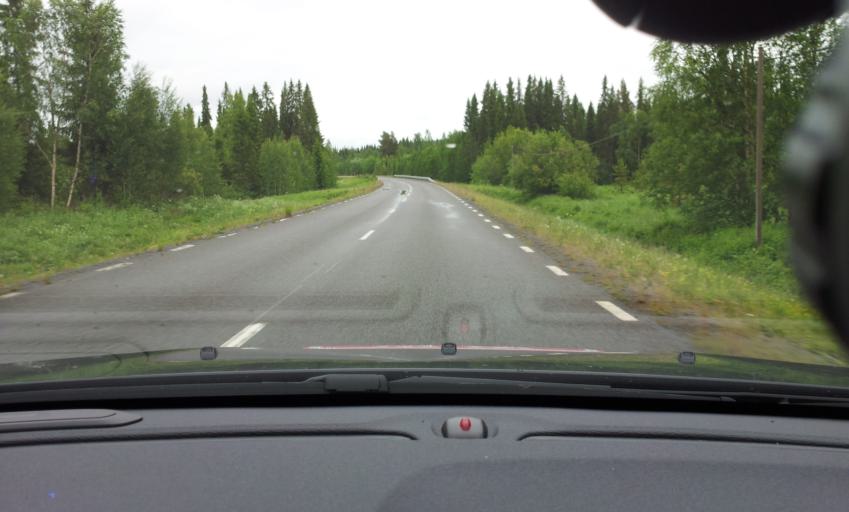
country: SE
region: Jaemtland
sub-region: OEstersunds Kommun
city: Lit
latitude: 63.6873
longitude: 15.0172
